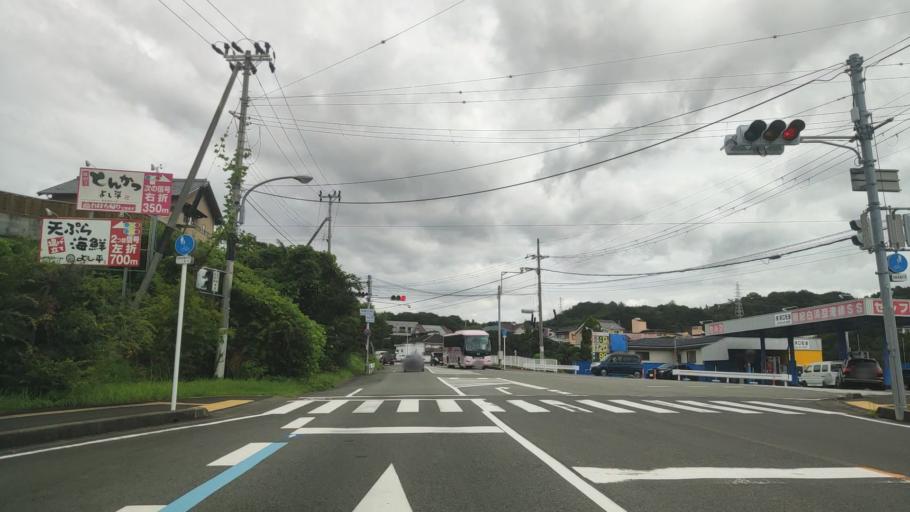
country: JP
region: Wakayama
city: Tanabe
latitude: 33.7058
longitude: 135.3986
